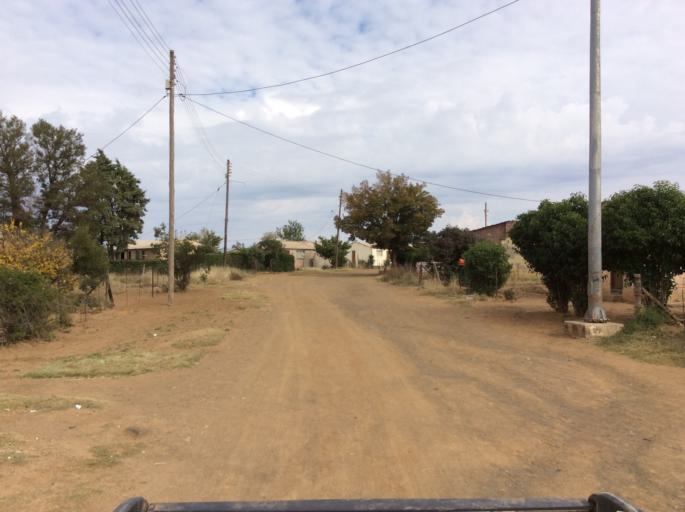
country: LS
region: Mafeteng
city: Mafeteng
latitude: -29.7234
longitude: 27.0105
